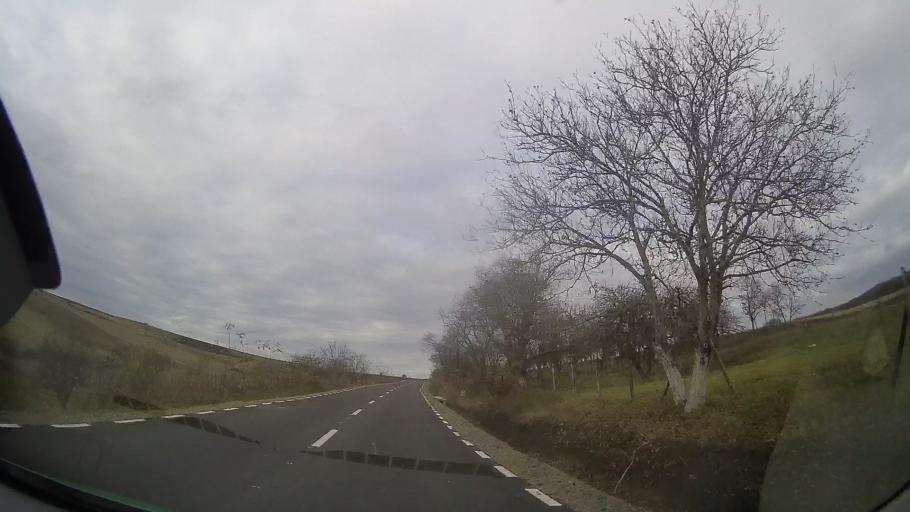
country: RO
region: Bistrita-Nasaud
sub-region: Comuna Teaca
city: Ocnita
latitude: 46.8233
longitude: 24.4815
